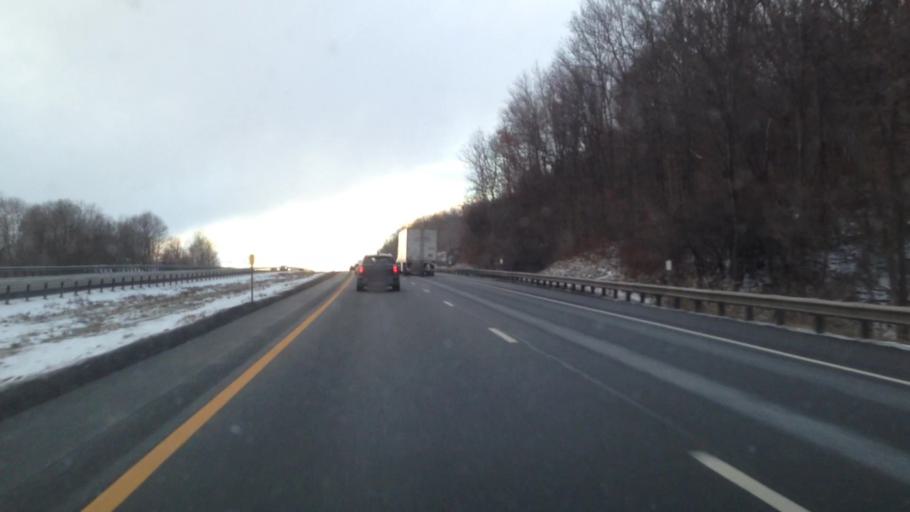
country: US
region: New York
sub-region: Herkimer County
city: Ilion
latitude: 43.0251
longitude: -75.0272
